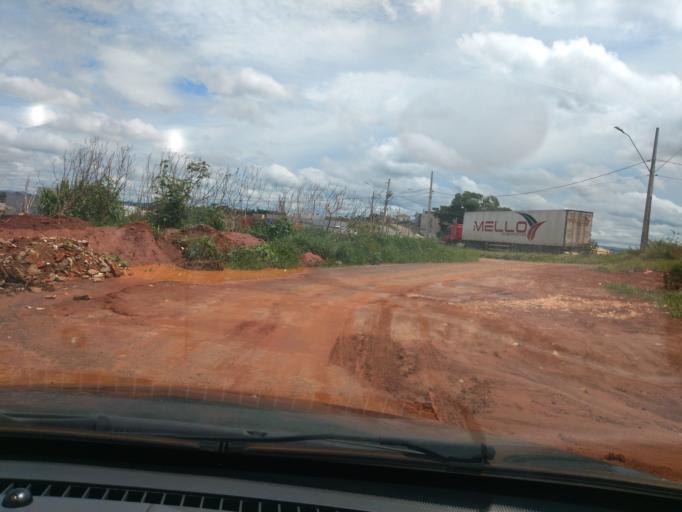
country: BR
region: Minas Gerais
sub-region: Tres Coracoes
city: Tres Coracoes
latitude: -21.6763
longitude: -45.2779
